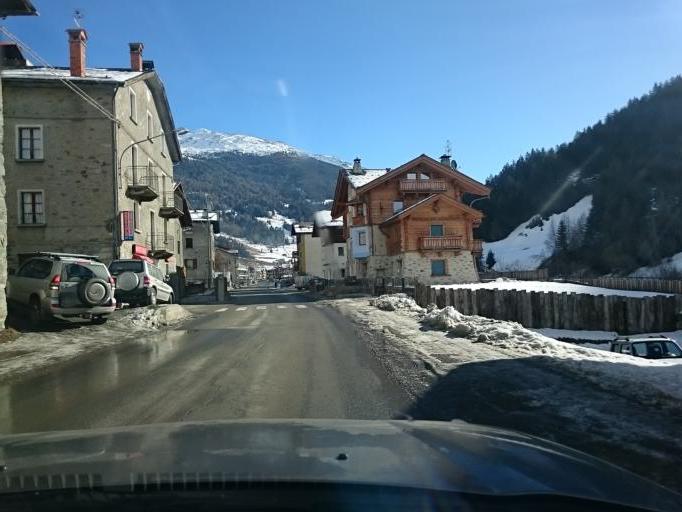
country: IT
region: Lombardy
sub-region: Provincia di Sondrio
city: Sant'Antonio
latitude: 46.4620
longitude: 10.4138
